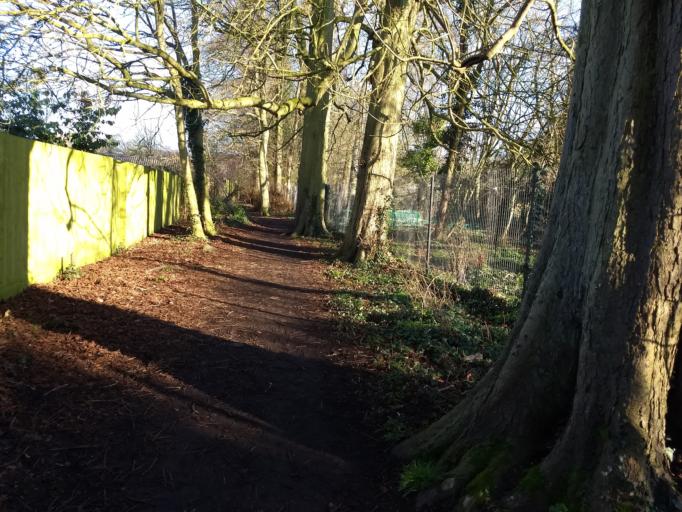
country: GB
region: England
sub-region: Buckinghamshire
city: Buckingham
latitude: 52.0069
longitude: -0.9797
